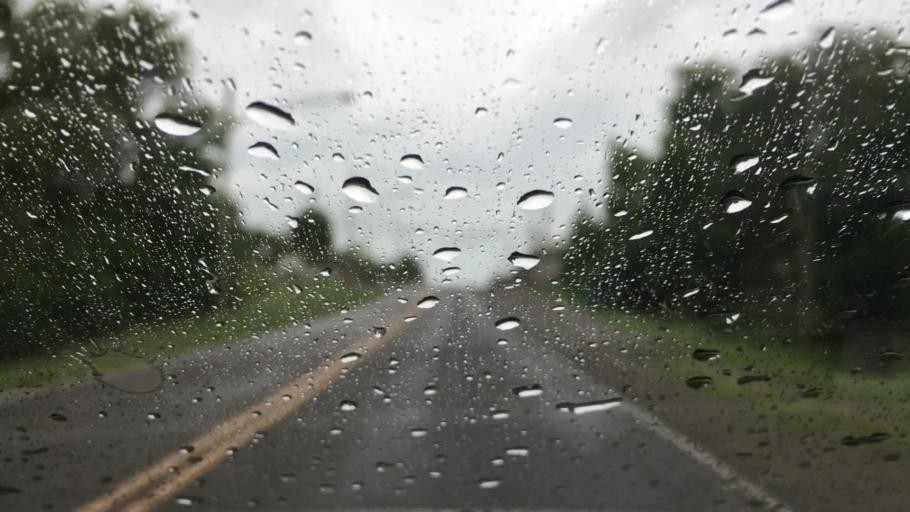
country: US
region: Oklahoma
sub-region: Cherokee County
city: Tahlequah
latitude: 35.9162
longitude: -94.9879
